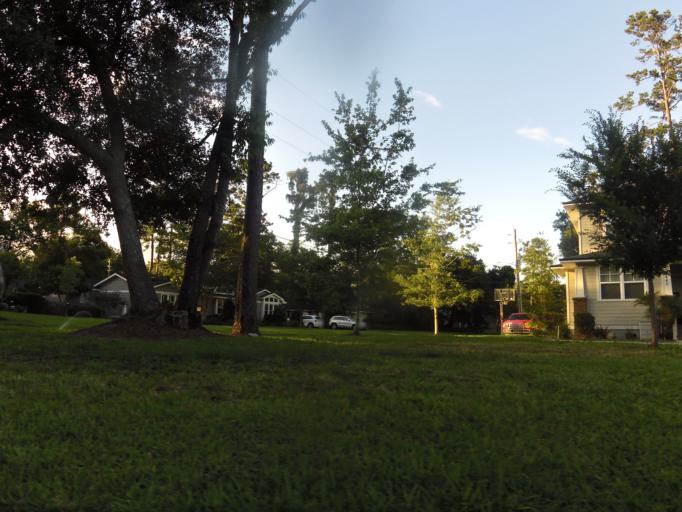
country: US
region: Florida
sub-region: Duval County
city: Jacksonville
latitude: 30.2669
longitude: -81.7054
